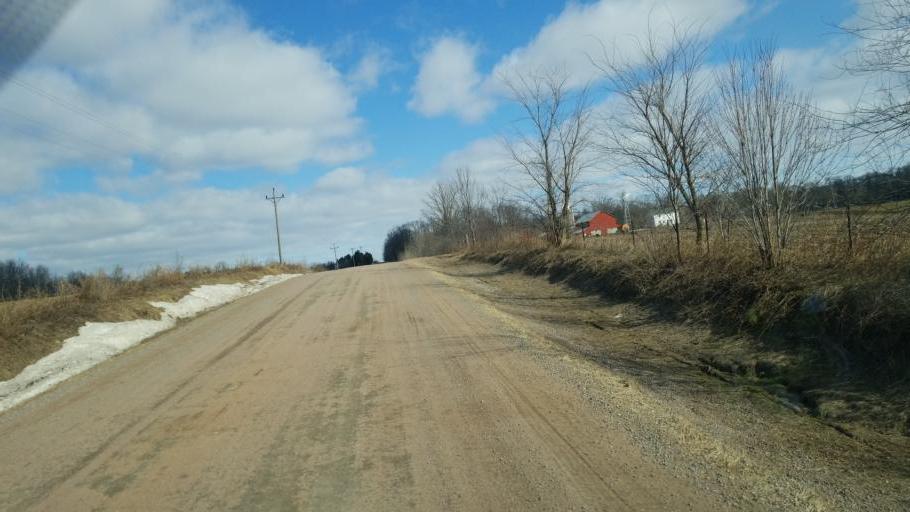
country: US
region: Wisconsin
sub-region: Clark County
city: Loyal
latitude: 44.6366
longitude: -90.4359
